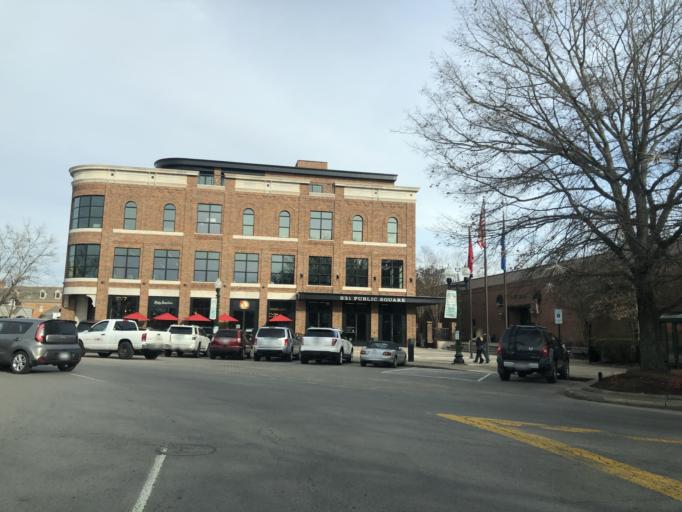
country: US
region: Tennessee
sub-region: Williamson County
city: Franklin
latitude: 35.9250
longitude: -86.8689
